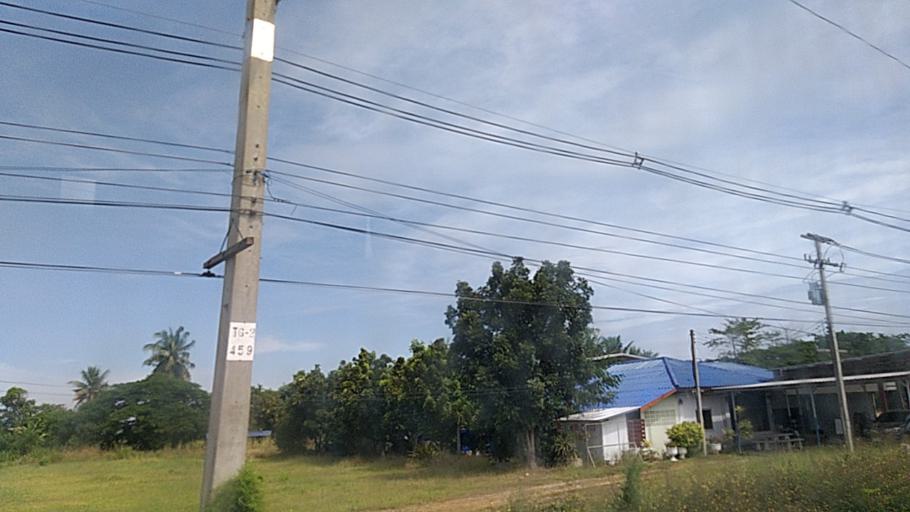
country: TH
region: Maha Sarakham
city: Chiang Yuen
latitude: 16.4427
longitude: 102.9876
